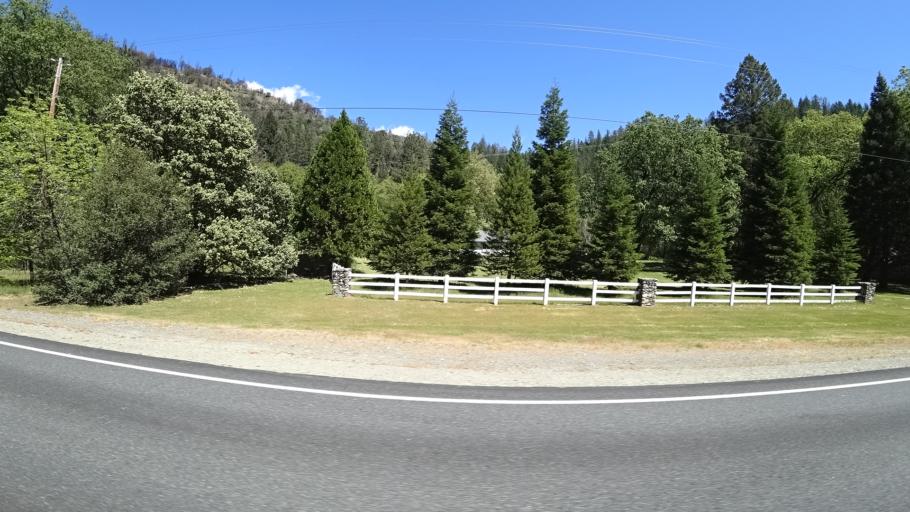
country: US
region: California
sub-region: Trinity County
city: Weaverville
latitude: 40.7552
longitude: -123.0661
